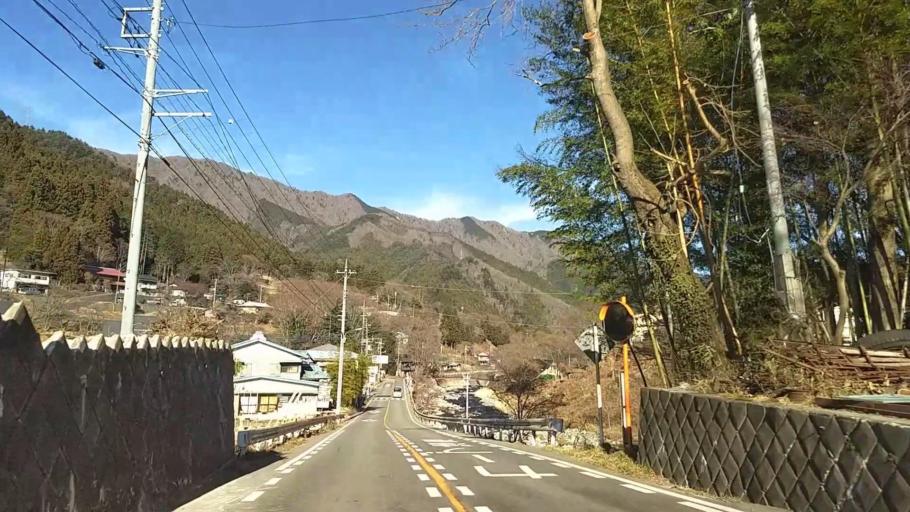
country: JP
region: Yamanashi
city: Otsuki
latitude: 35.5190
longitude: 139.0200
